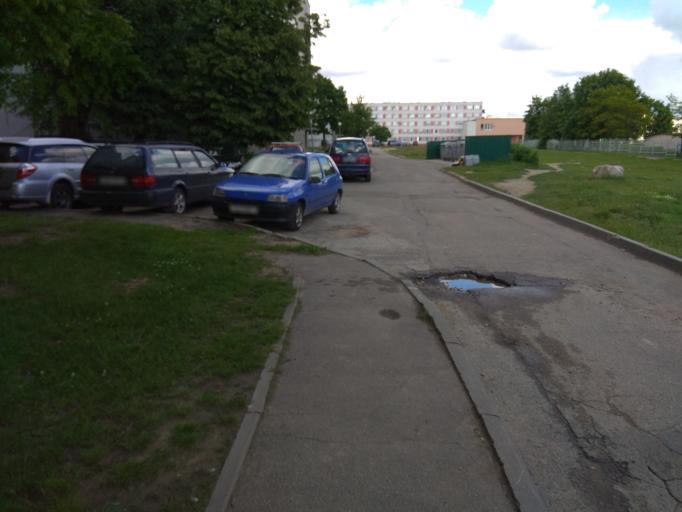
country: BY
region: Grodnenskaya
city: Hrodna
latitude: 53.7095
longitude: 23.8069
